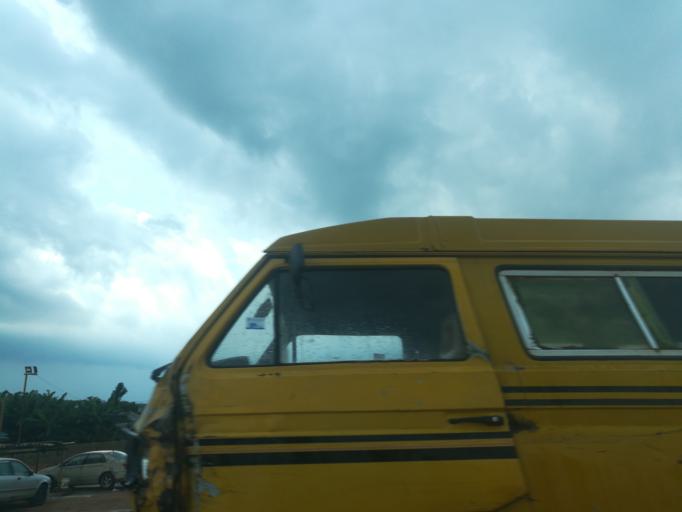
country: NG
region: Lagos
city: Ikorodu
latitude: 6.6614
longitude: 3.5915
